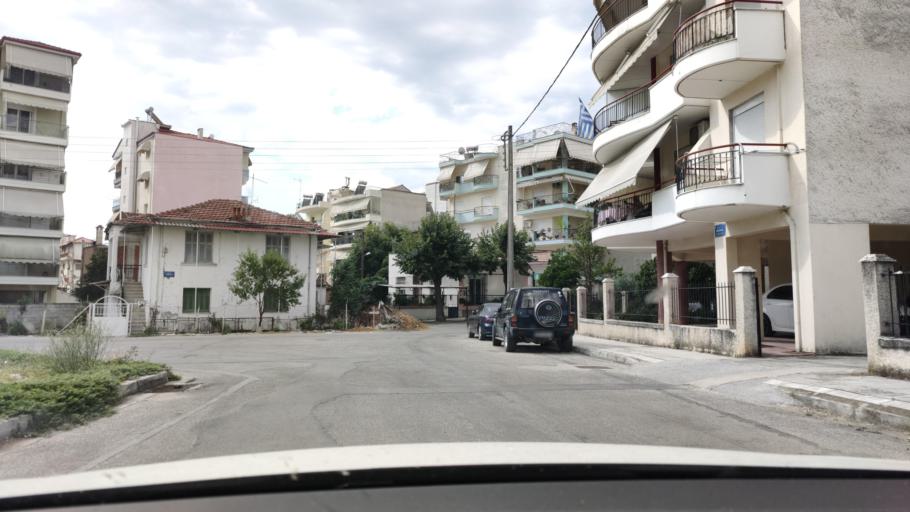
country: GR
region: Central Macedonia
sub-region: Nomos Serron
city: Serres
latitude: 41.0854
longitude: 23.5363
